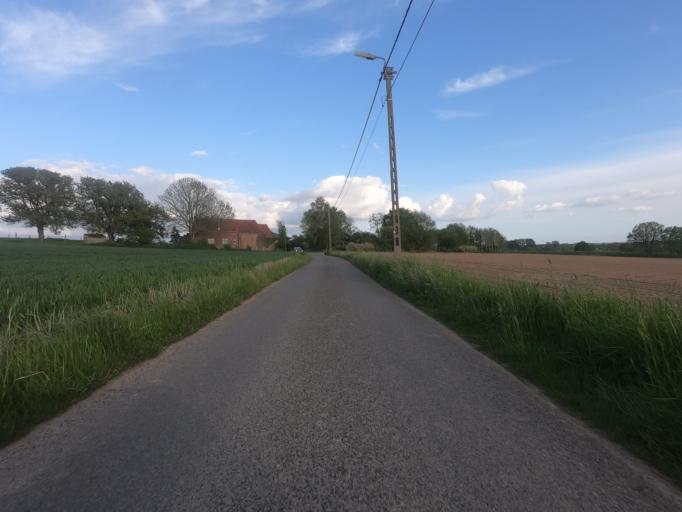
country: BE
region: Flanders
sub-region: Provincie Vlaams-Brabant
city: Herne
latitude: 50.7556
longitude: 4.0140
